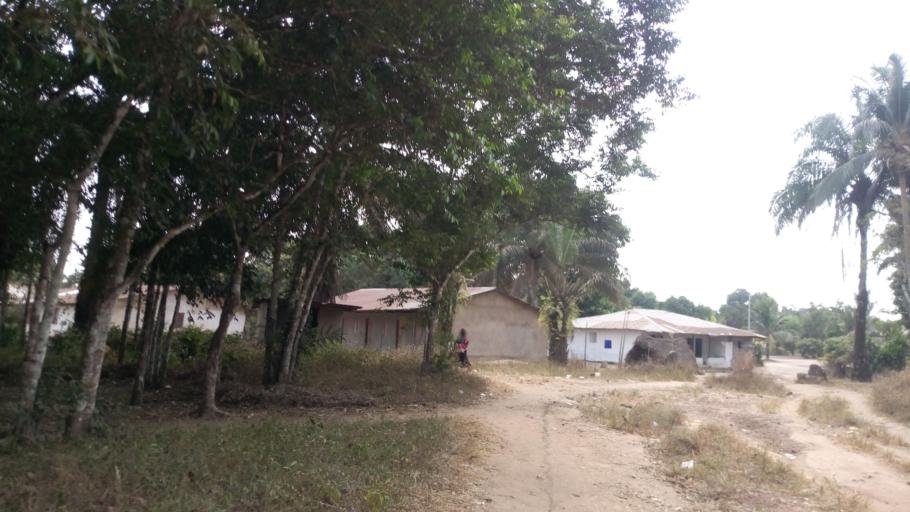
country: SL
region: Southern Province
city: Mogbwemo
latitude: 7.7885
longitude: -12.3019
